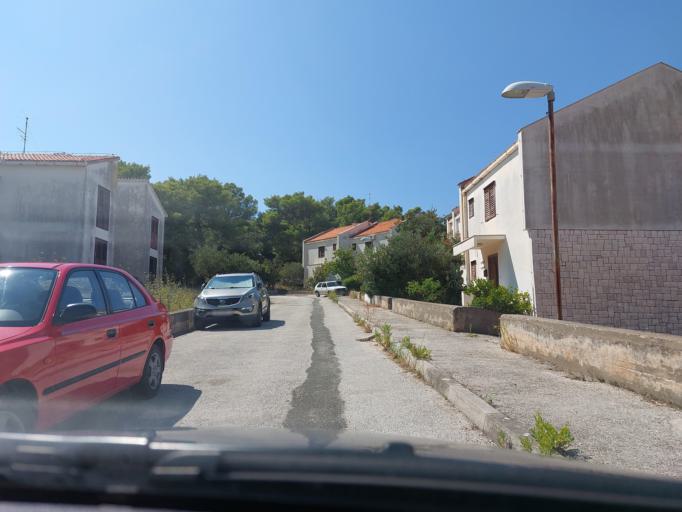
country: HR
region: Dubrovacko-Neretvanska
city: Smokvica
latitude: 42.7431
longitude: 16.8260
